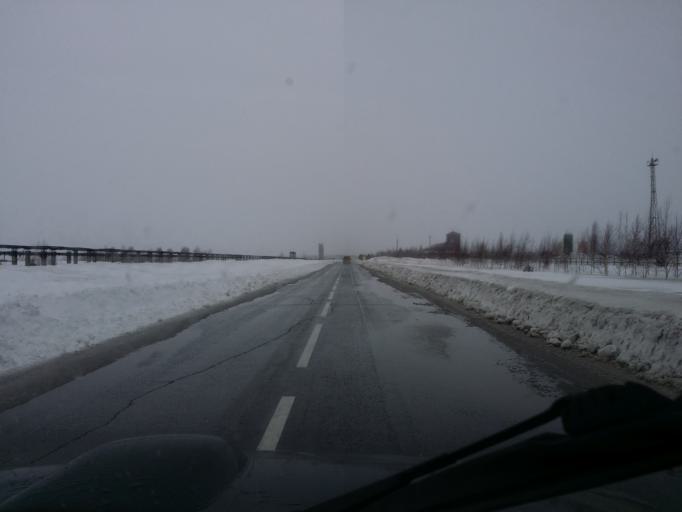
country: RU
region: Khanty-Mansiyskiy Avtonomnyy Okrug
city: Izluchinsk
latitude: 60.9765
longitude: 76.9296
